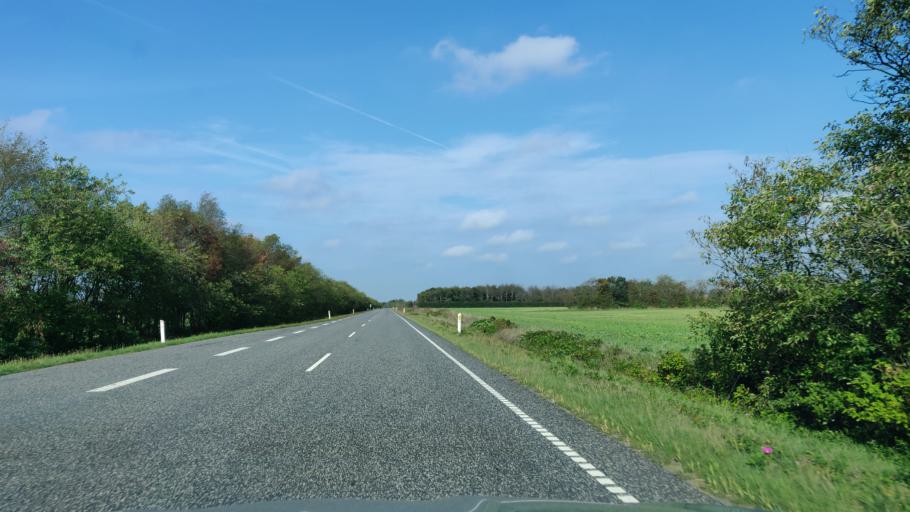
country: DK
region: Central Jutland
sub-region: Herning Kommune
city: Sunds
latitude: 56.2458
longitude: 9.0738
